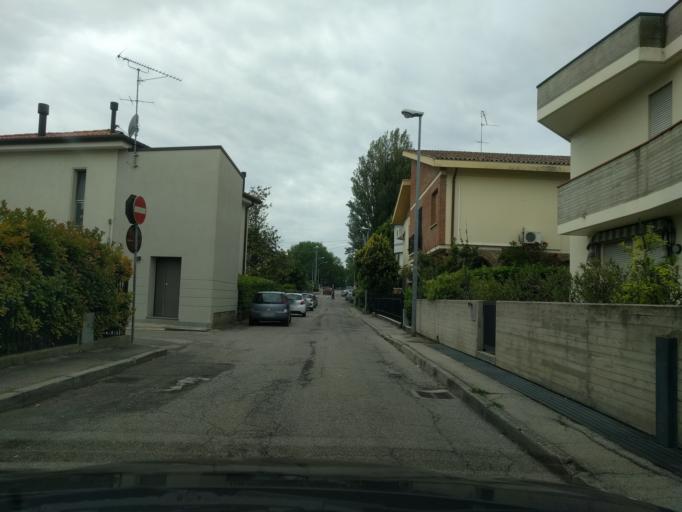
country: IT
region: Veneto
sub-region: Provincia di Rovigo
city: Rovigo
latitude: 45.0693
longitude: 11.7847
